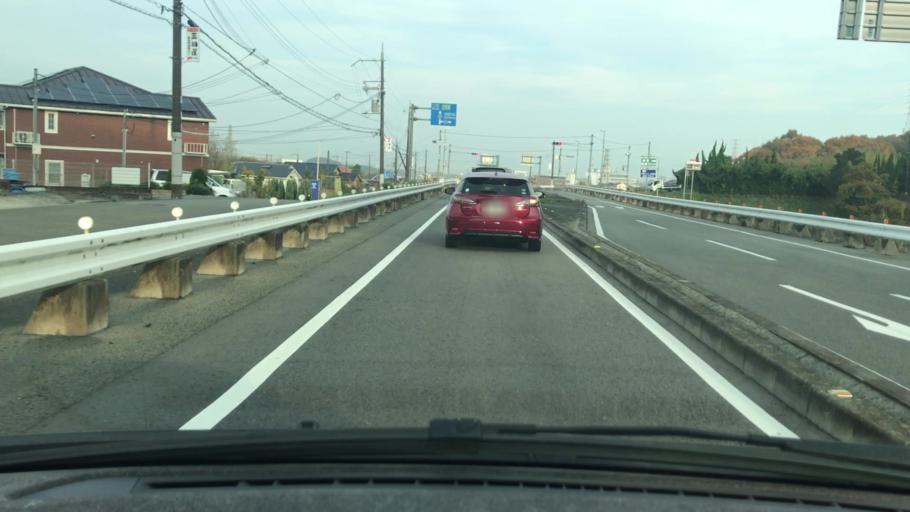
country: JP
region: Hyogo
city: Sandacho
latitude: 34.8184
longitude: 135.2496
